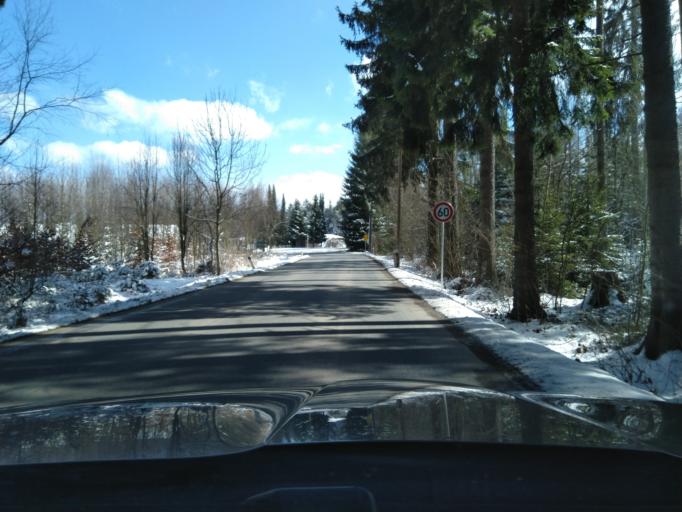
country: CZ
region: Jihocesky
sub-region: Okres Prachatice
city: Zdikov
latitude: 49.0625
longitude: 13.7357
